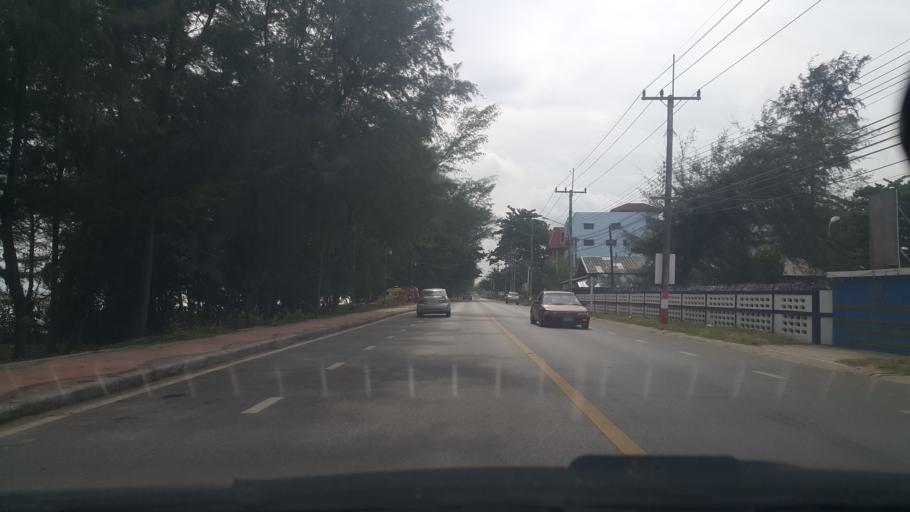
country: TH
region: Rayong
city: Rayong
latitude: 12.6280
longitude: 101.3516
